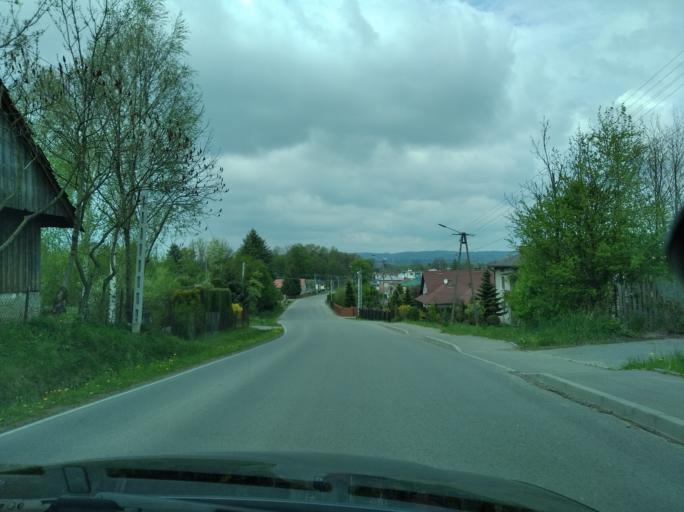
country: PL
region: Subcarpathian Voivodeship
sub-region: Powiat brzozowski
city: Haczow
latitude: 49.6671
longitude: 21.8978
